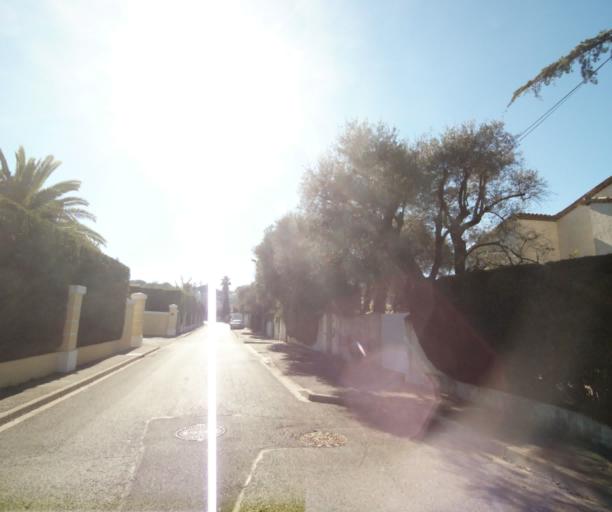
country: FR
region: Provence-Alpes-Cote d'Azur
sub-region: Departement des Alpes-Maritimes
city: Antibes
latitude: 43.5538
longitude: 7.1253
